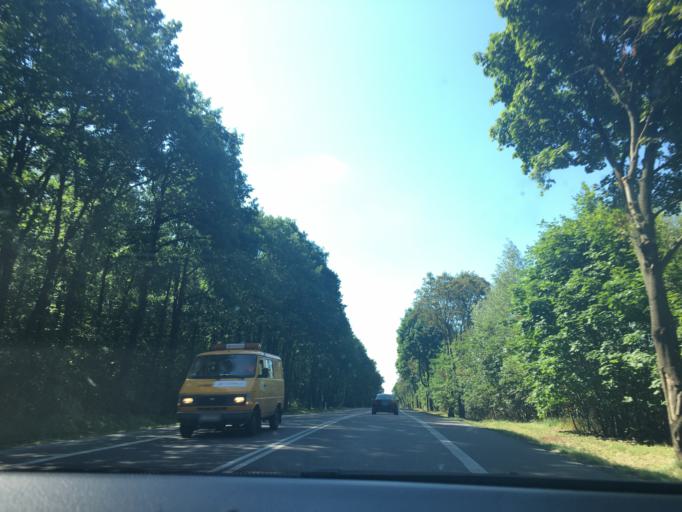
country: PL
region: Lublin Voivodeship
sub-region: Powiat lubelski
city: Niemce
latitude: 51.3959
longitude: 22.6366
